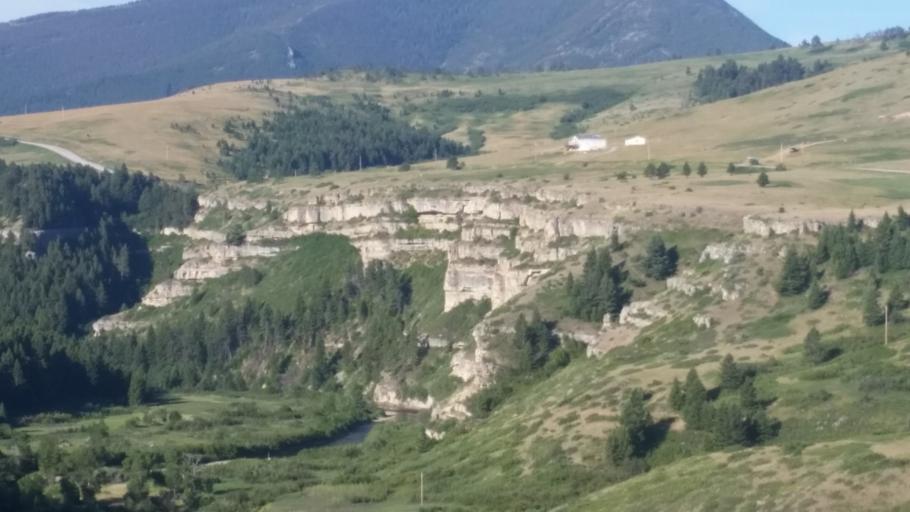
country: US
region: Montana
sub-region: Cascade County
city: Malmstrom Air Force Base
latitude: 47.2104
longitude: -110.9299
